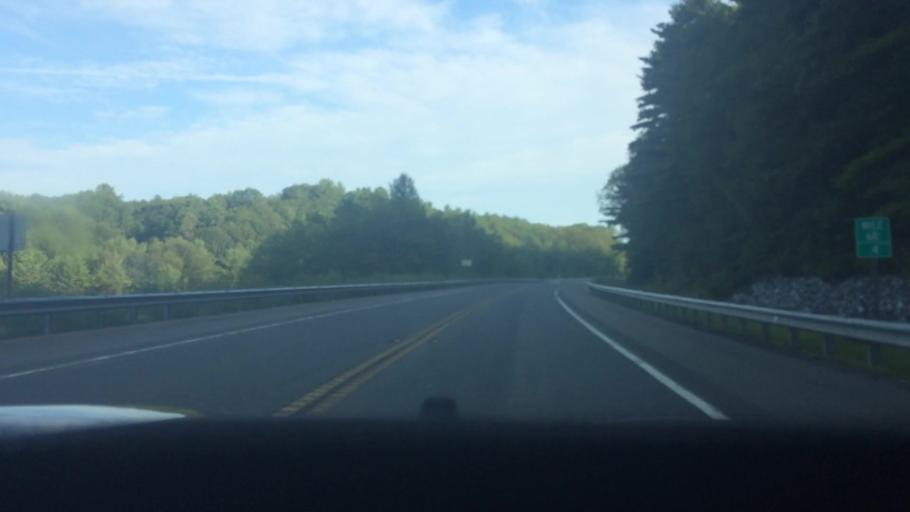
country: US
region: Massachusetts
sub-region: Franklin County
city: Orange
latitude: 42.5711
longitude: -72.3210
